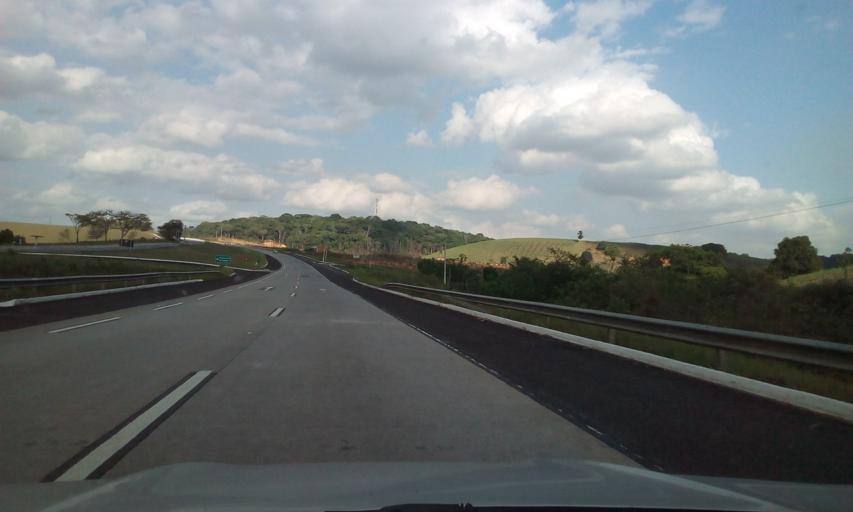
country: BR
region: Pernambuco
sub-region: Joaquim Nabuco
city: Joaquim Nabuco
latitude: -8.5881
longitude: -35.5047
